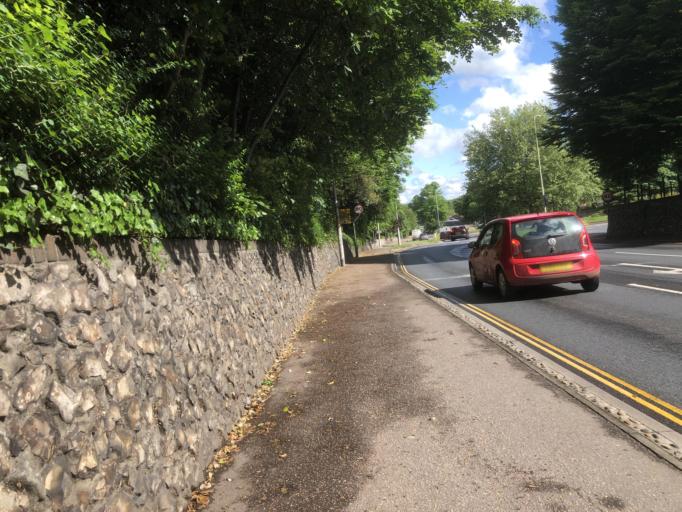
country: GB
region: England
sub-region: Norfolk
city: Thorpe Hamlet
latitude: 52.6167
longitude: 1.3096
